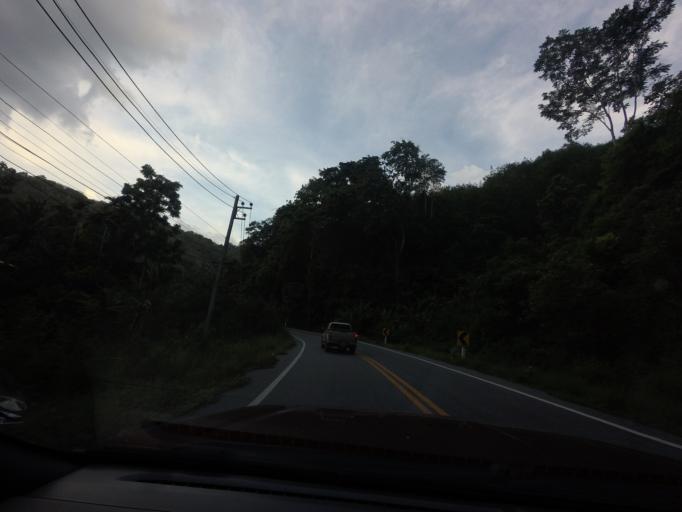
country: TH
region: Yala
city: Than To
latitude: 6.0370
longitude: 101.1959
